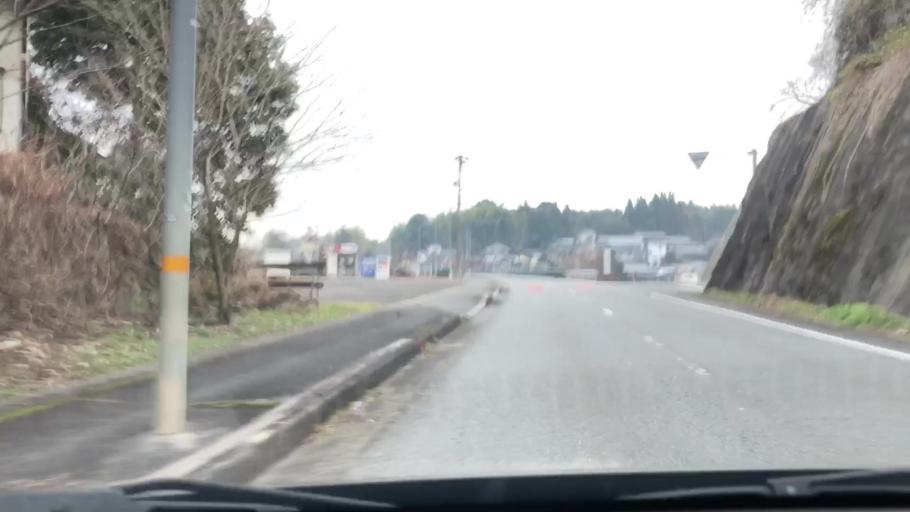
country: JP
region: Oita
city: Usuki
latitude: 33.0136
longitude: 131.6655
